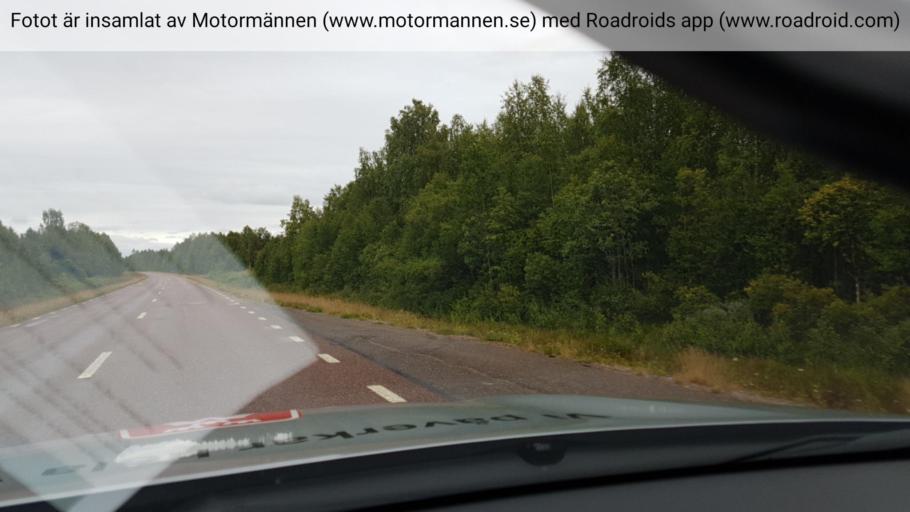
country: SE
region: Norrbotten
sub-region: Pajala Kommun
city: Pajala
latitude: 67.1498
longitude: 22.6265
